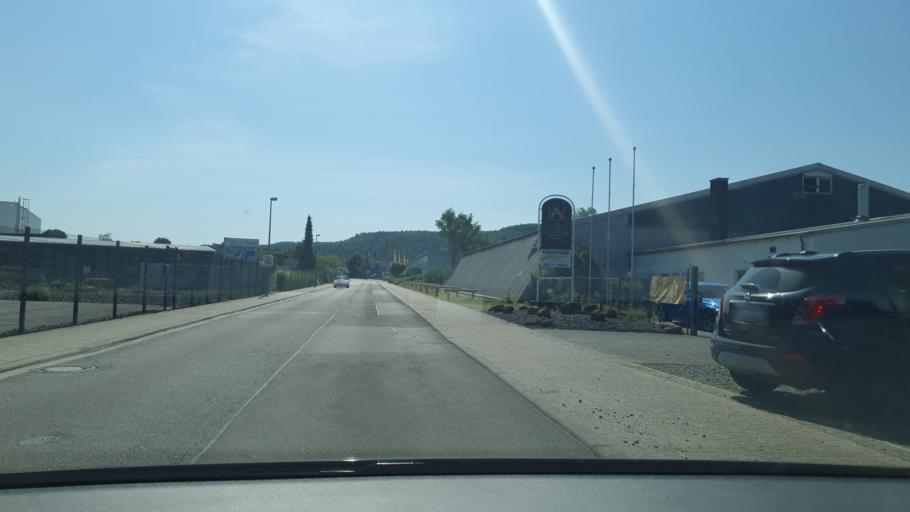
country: DE
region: Rheinland-Pfalz
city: Landstuhl
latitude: 49.4185
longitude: 7.5678
